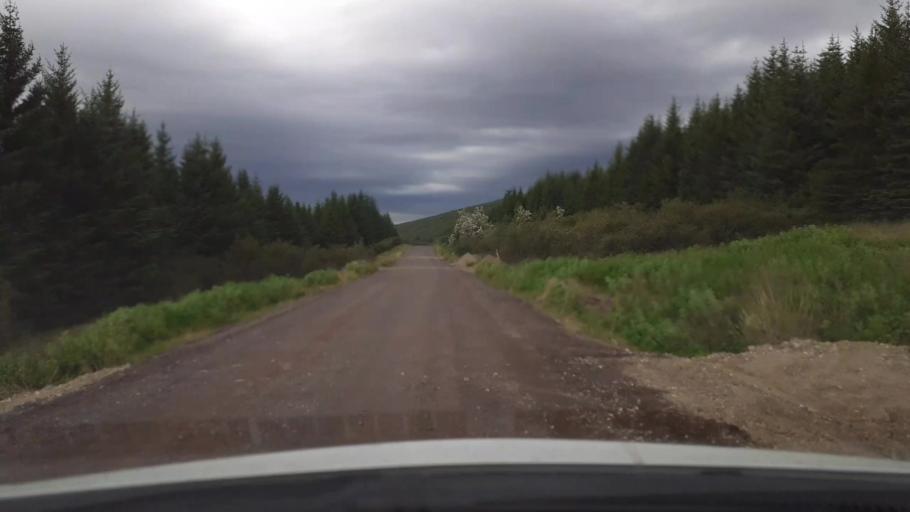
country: IS
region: West
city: Borgarnes
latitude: 64.5364
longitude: -21.5241
